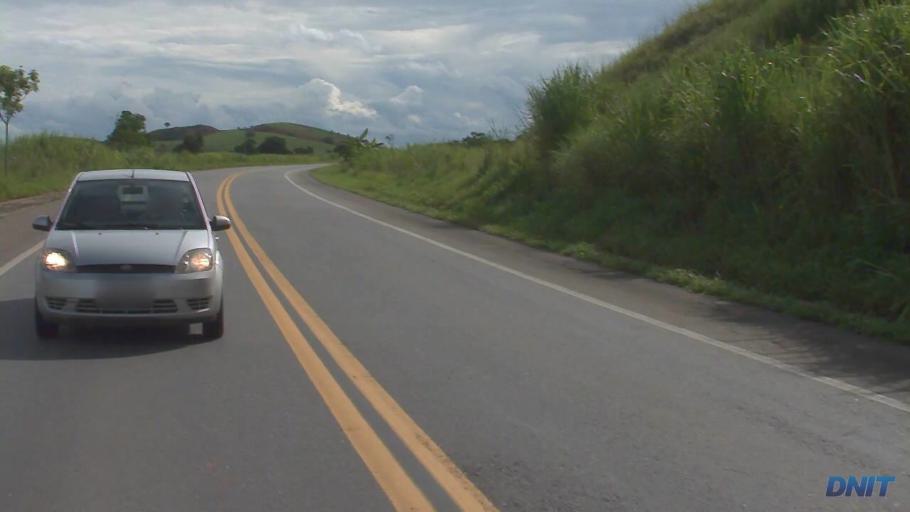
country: BR
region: Minas Gerais
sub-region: Belo Oriente
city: Belo Oriente
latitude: -19.1929
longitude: -42.2767
